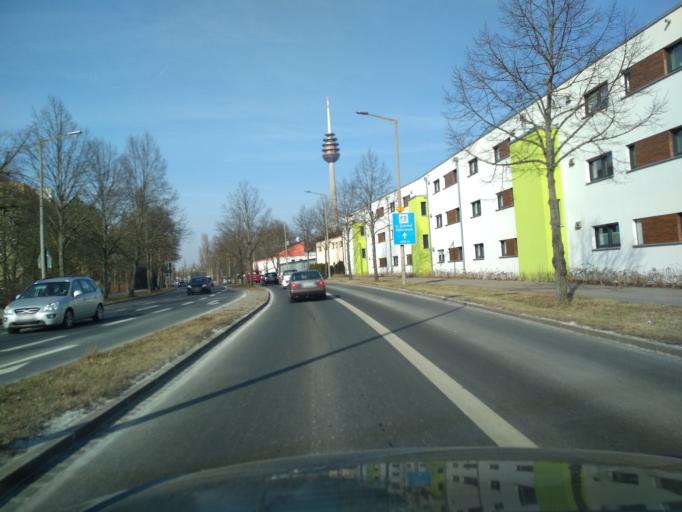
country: DE
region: Bavaria
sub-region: Regierungsbezirk Mittelfranken
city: Stein
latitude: 49.4170
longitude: 11.0365
